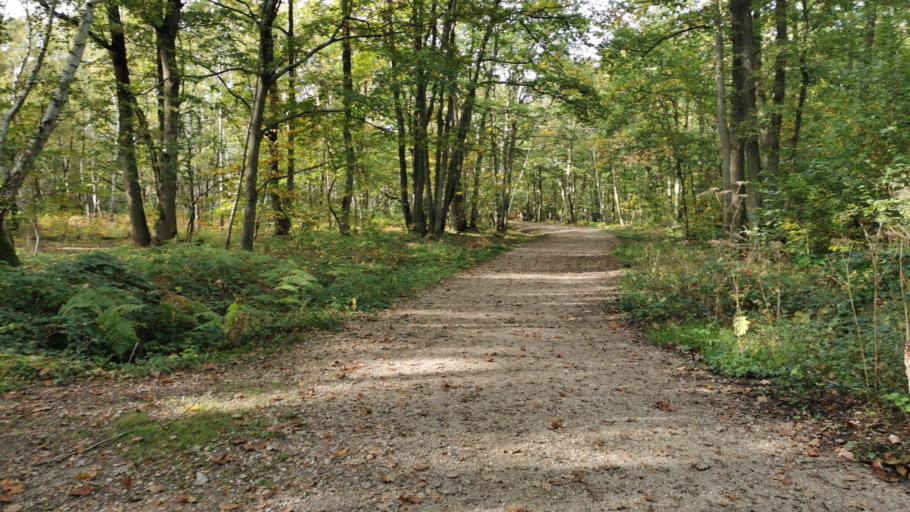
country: FR
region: Ile-de-France
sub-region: Departement des Yvelines
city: Neauphle-le-Chateau
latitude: 48.8016
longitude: 1.9210
